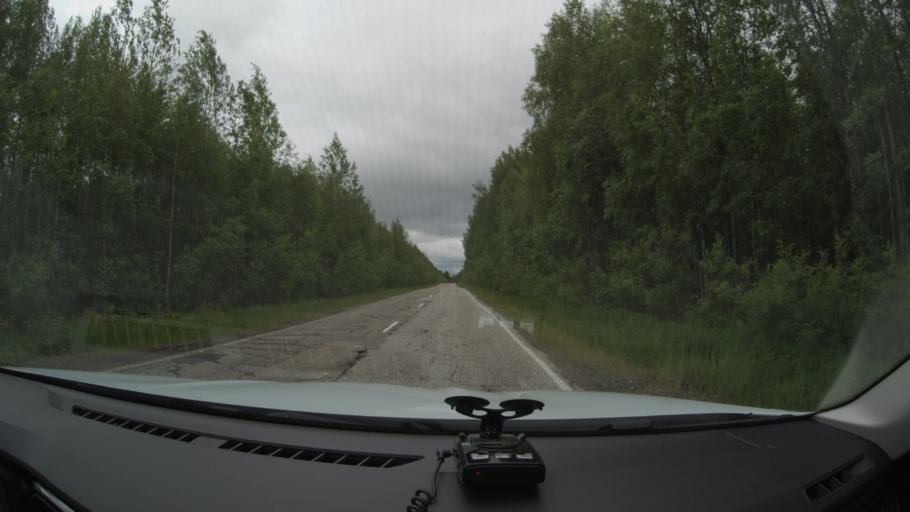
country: RU
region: Komi Republic
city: Nizhniy Odes
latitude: 63.6047
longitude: 54.5197
